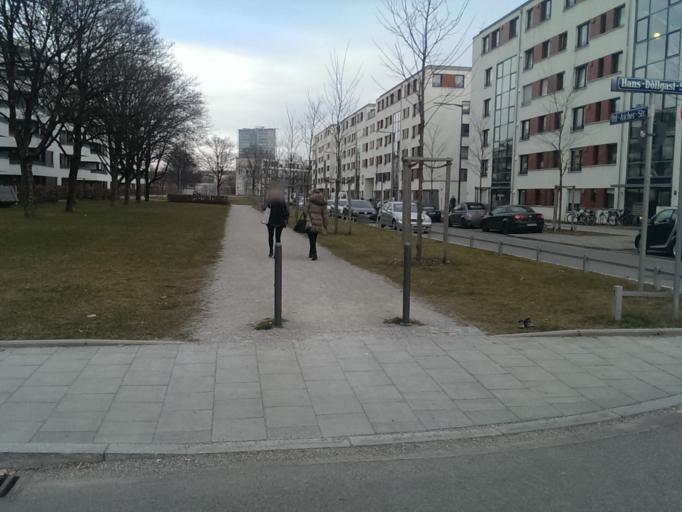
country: DE
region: Bavaria
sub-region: Upper Bavaria
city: Bogenhausen
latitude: 48.1819
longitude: 11.5868
